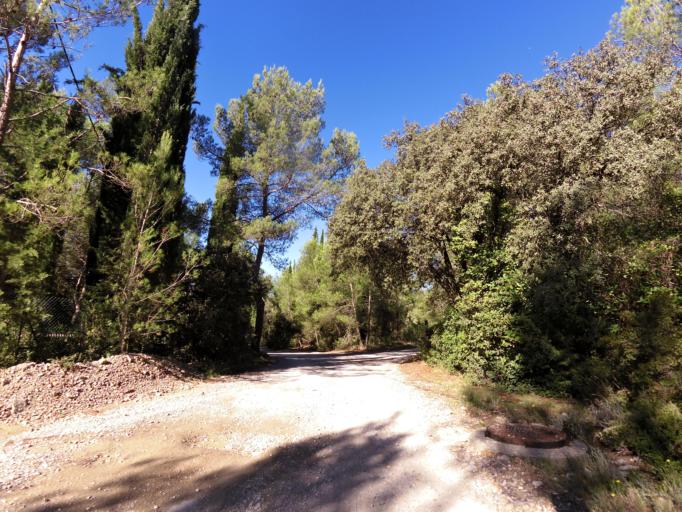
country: FR
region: Languedoc-Roussillon
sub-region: Departement du Gard
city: Aubais
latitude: 43.7424
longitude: 4.1502
